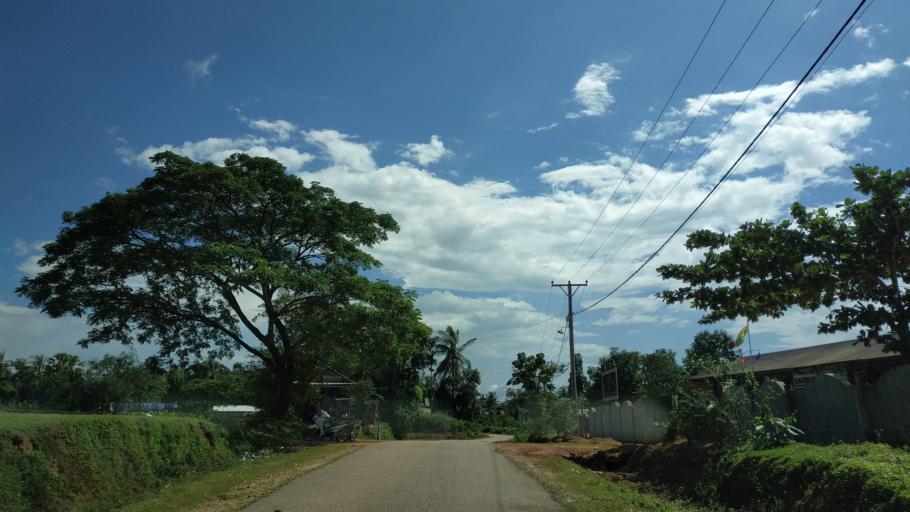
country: MM
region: Tanintharyi
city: Dawei
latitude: 14.2178
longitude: 98.1940
